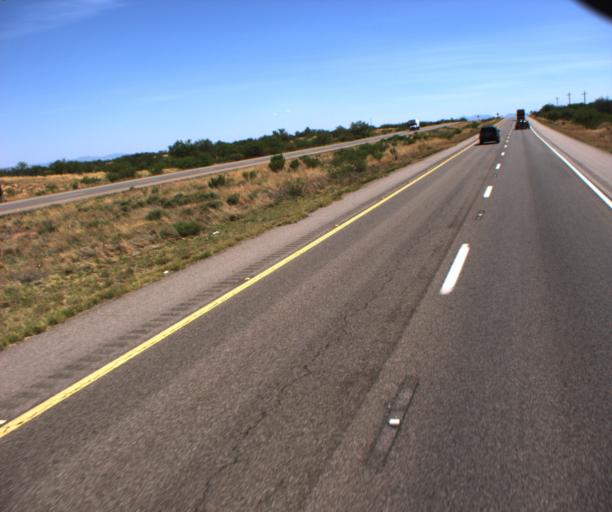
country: US
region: Arizona
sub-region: Cochise County
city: Whetstone
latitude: 31.8869
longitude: -110.3413
